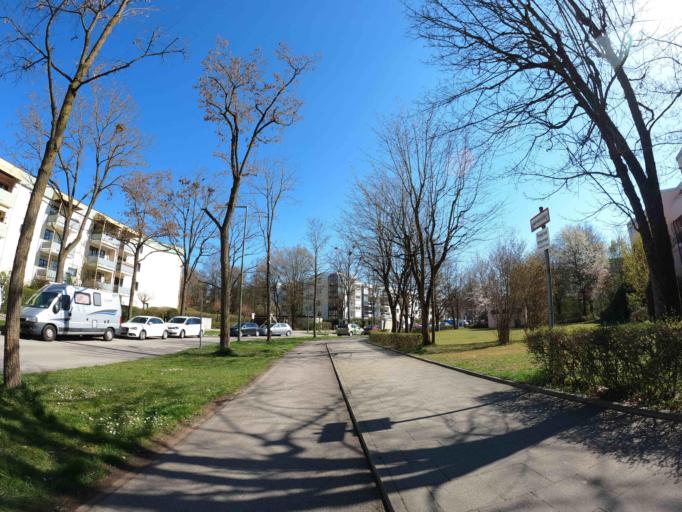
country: DE
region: Bavaria
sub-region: Upper Bavaria
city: Neubiberg
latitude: 48.0867
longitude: 11.6399
